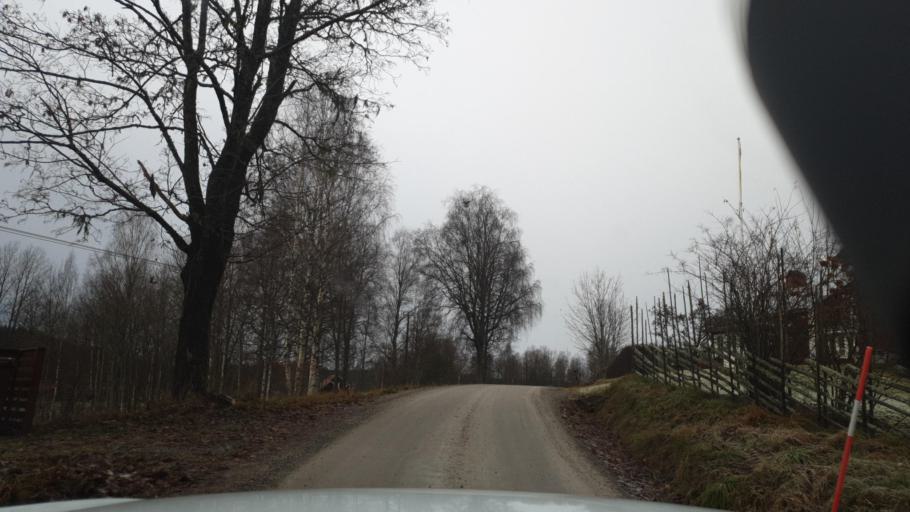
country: SE
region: Vaermland
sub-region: Arvika Kommun
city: Arvika
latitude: 59.7159
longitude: 12.8450
